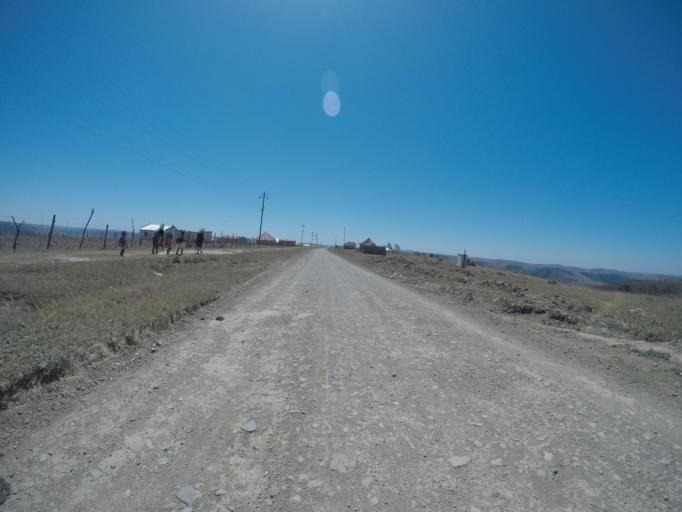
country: ZA
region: Eastern Cape
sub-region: OR Tambo District Municipality
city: Mthatha
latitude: -31.8846
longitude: 28.8751
